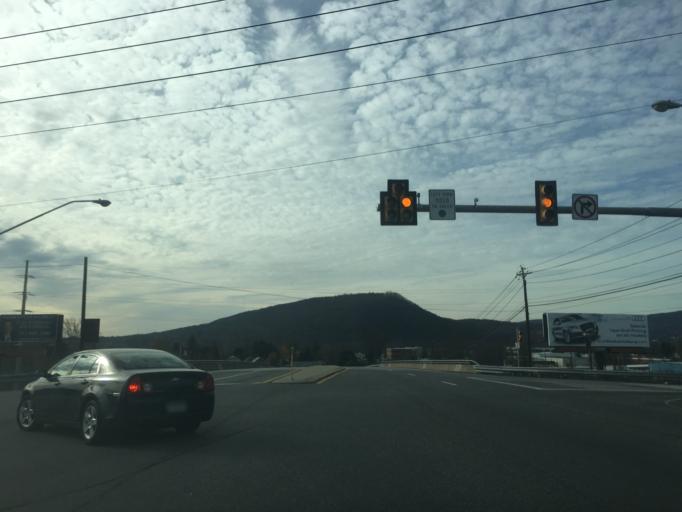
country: US
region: Pennsylvania
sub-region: Perry County
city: Marysville
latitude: 40.3261
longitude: -76.8922
